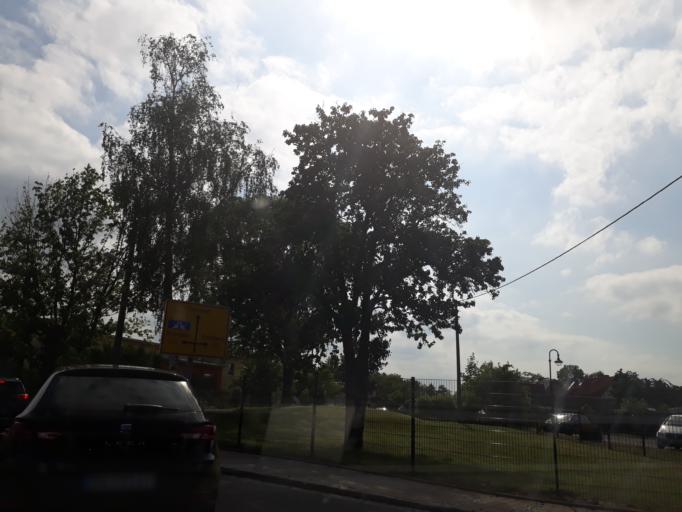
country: DE
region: Saxony
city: Wilsdruff
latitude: 51.0327
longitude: 13.5481
